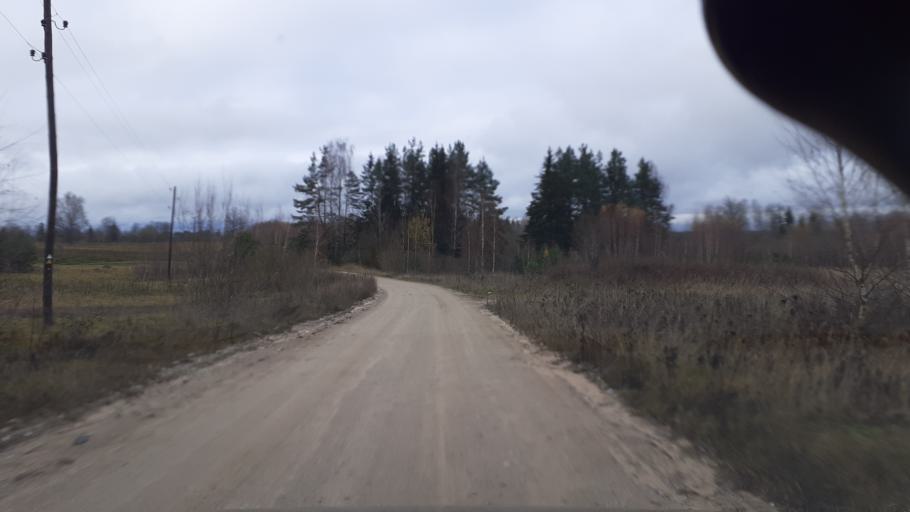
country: LV
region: Kuldigas Rajons
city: Kuldiga
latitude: 57.0390
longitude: 21.8798
